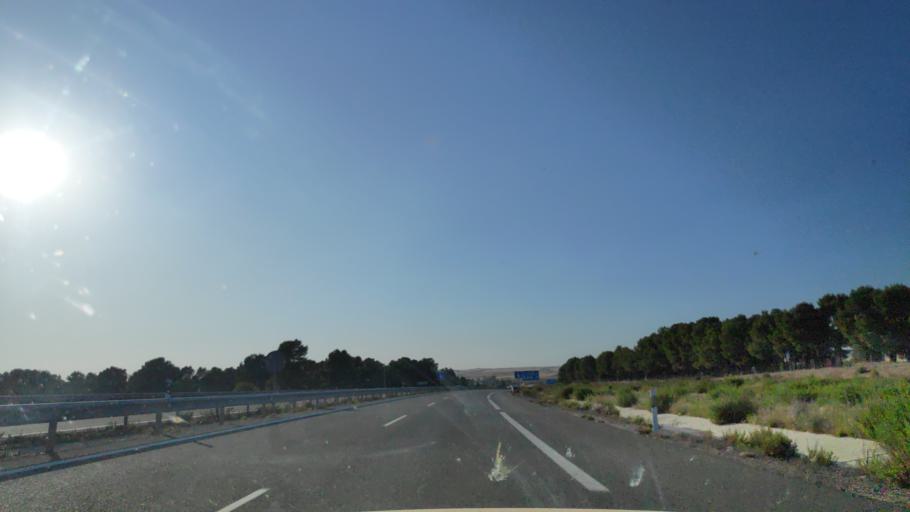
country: ES
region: Castille-La Mancha
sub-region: Provincia de Cuenca
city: Montalbo
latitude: 39.8951
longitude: -2.7039
